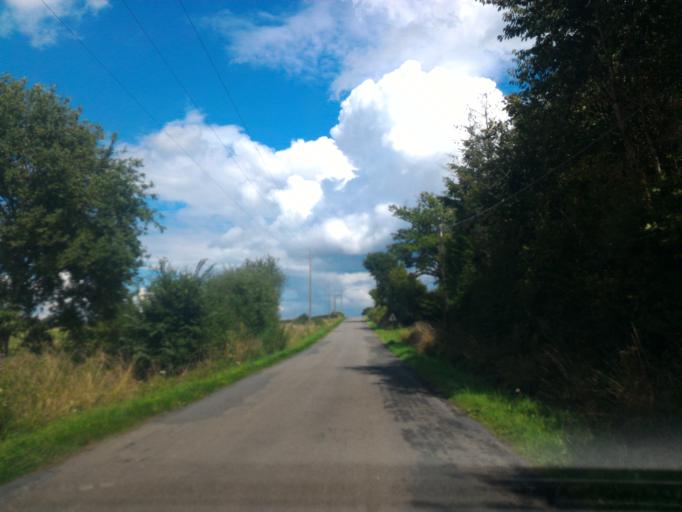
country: FR
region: Poitou-Charentes
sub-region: Departement de la Charente
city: Brigueuil
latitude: 45.9547
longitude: 0.8102
